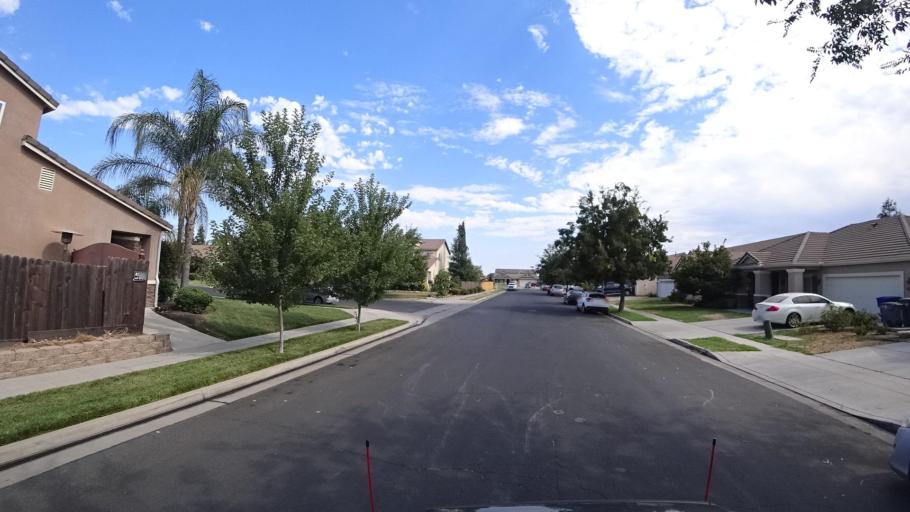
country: US
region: California
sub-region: Fresno County
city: Tarpey Village
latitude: 36.7816
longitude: -119.6772
